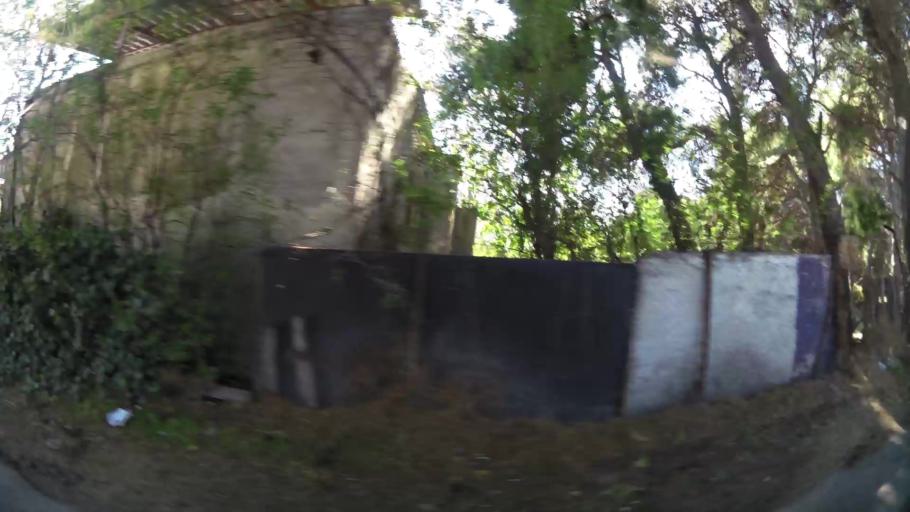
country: GR
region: Attica
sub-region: Nomarchia Athinas
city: Lykovrysi
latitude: 38.0816
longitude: 23.7801
